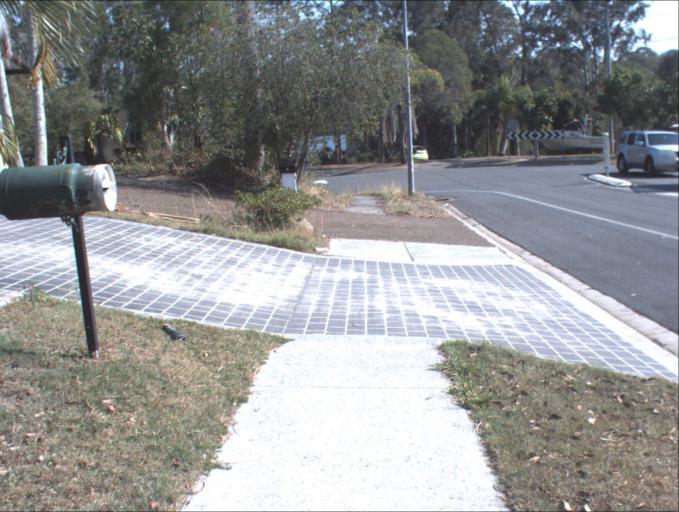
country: AU
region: Queensland
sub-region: Logan
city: Beenleigh
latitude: -27.6969
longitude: 153.1772
